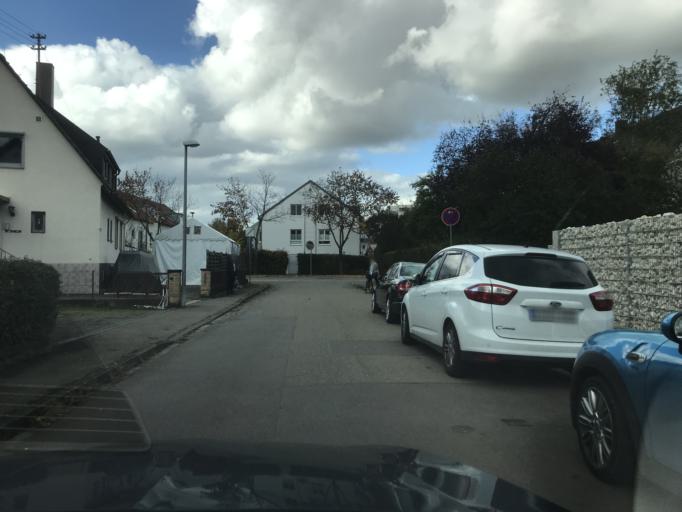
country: DE
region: Baden-Wuerttemberg
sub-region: Regierungsbezirk Stuttgart
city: Wendlingen am Neckar
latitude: 48.6711
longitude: 9.3817
